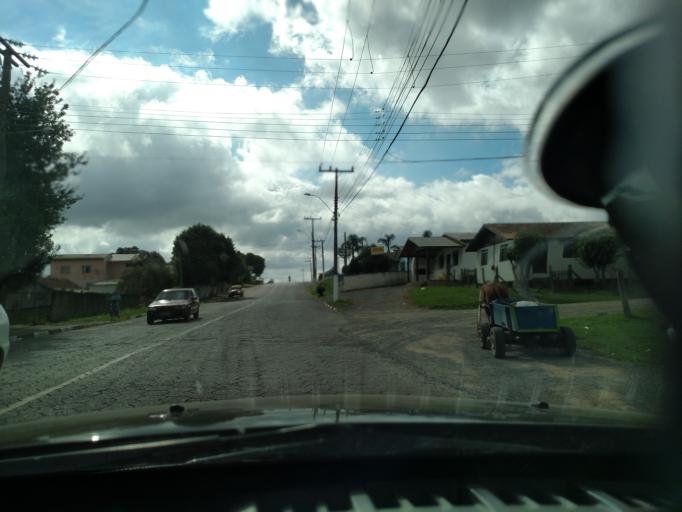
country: BR
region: Santa Catarina
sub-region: Lages
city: Lages
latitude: -27.8151
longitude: -50.2843
